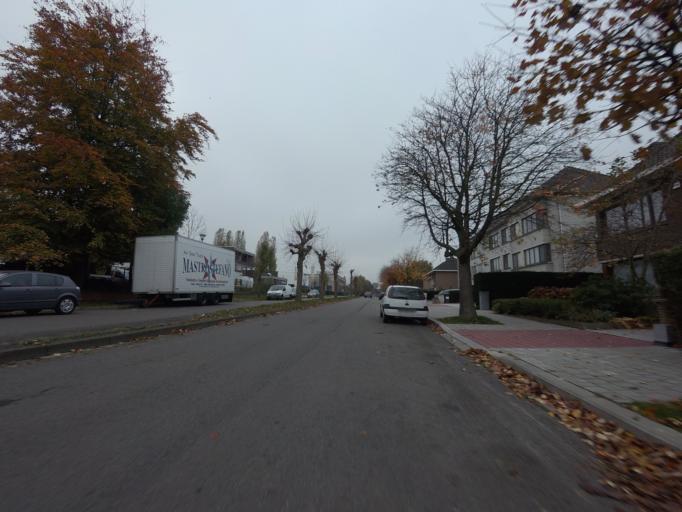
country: BE
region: Flanders
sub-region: Provincie Vlaams-Brabant
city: Diegem
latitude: 50.8652
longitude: 4.4343
